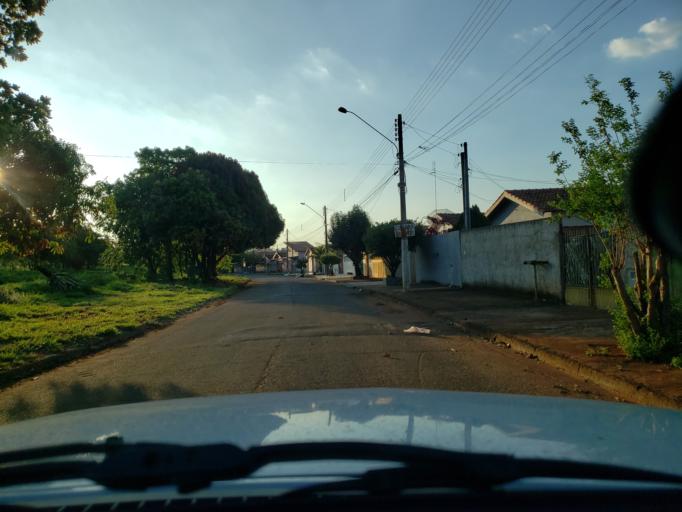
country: BR
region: Sao Paulo
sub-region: Moji-Guacu
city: Mogi-Gaucu
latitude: -22.3429
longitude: -46.9356
